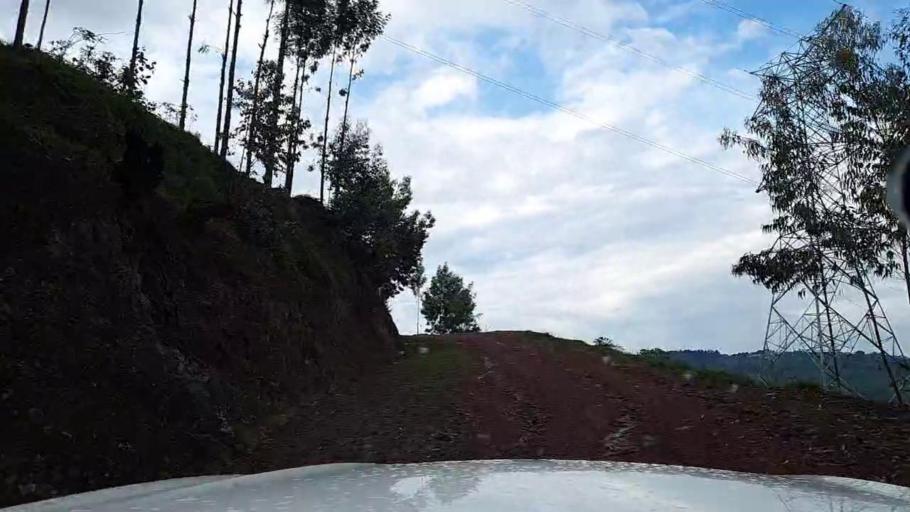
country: RW
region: Northern Province
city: Byumba
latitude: -1.7188
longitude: 29.9118
